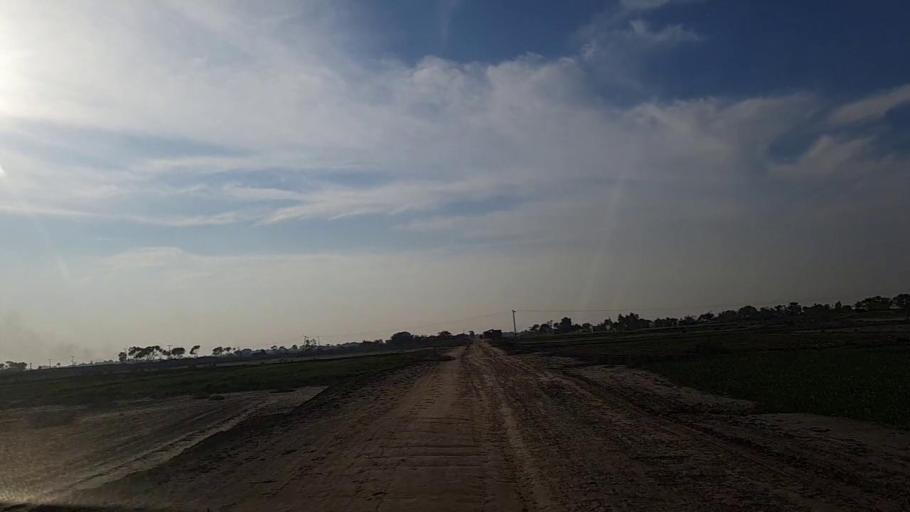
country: PK
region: Sindh
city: Bandhi
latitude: 26.5533
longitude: 68.2537
